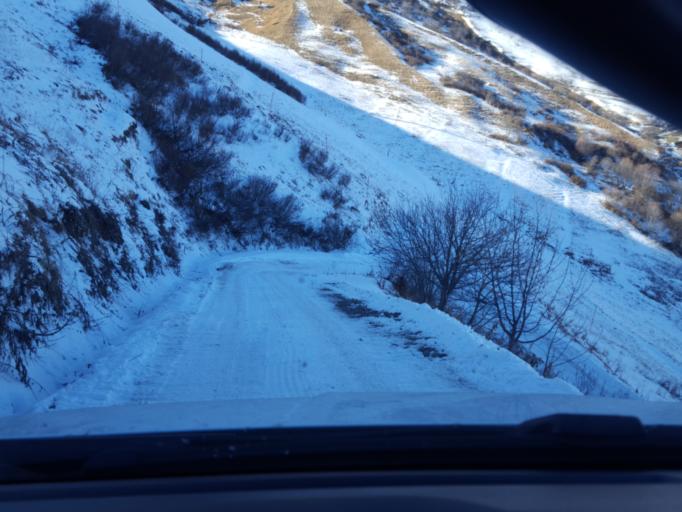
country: FR
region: Rhone-Alpes
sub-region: Departement de la Savoie
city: Saint-Jean-de-Maurienne
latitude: 45.2357
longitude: 6.2616
